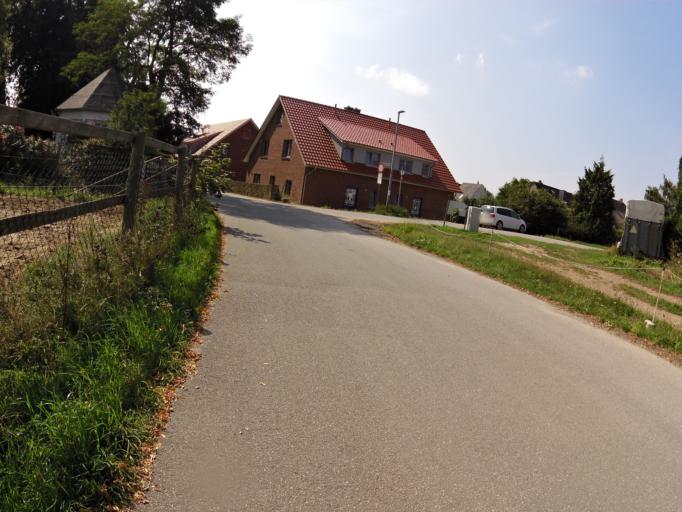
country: DE
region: Lower Saxony
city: Riede
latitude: 53.0141
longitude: 8.8879
